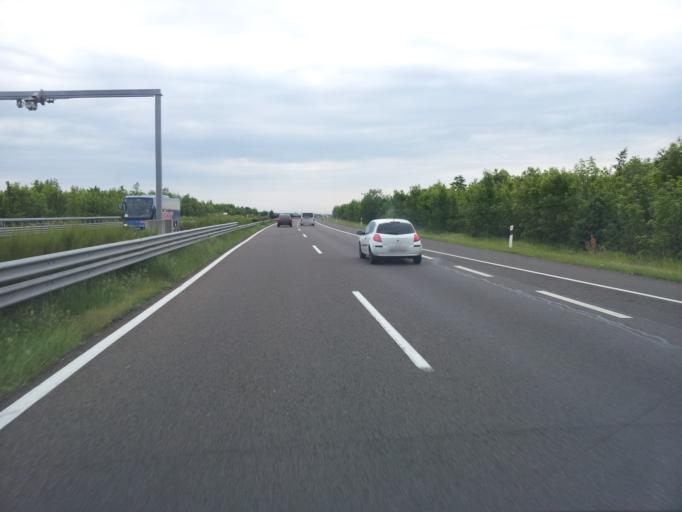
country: HU
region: Heves
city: Gyongyoshalasz
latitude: 47.7318
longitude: 19.9624
